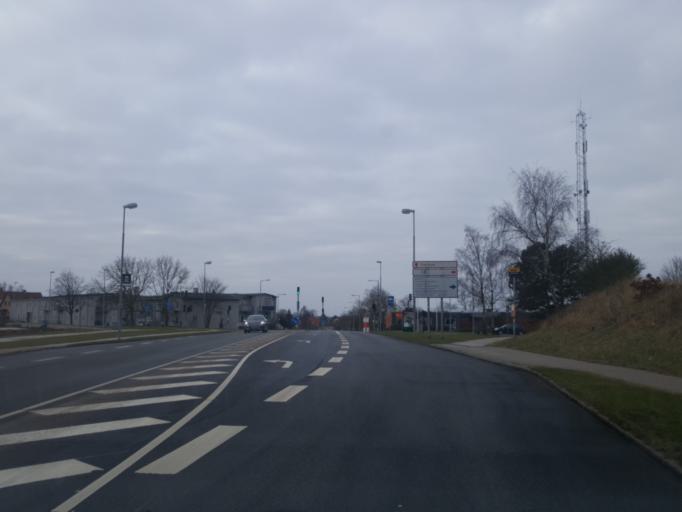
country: DK
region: Zealand
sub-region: Vordingborg Kommune
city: Vordingborg
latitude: 55.0140
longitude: 11.9203
